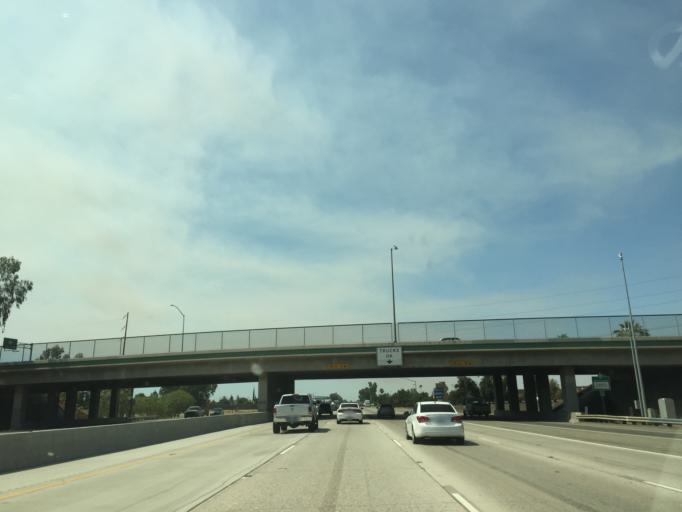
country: US
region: California
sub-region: Kern County
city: Greenfield
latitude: 35.2952
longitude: -119.0302
